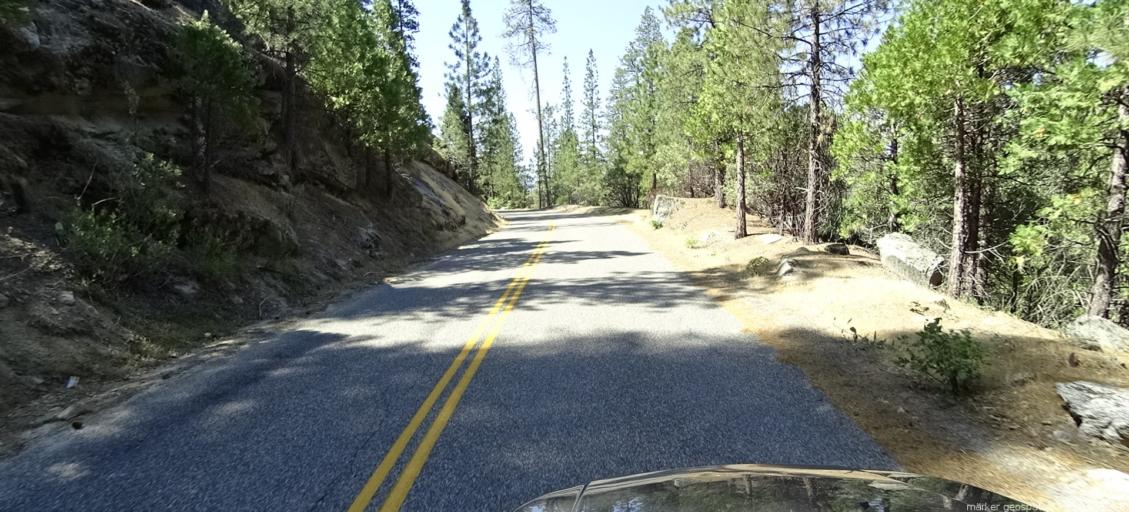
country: US
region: California
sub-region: Madera County
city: Oakhurst
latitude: 37.3869
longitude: -119.3640
